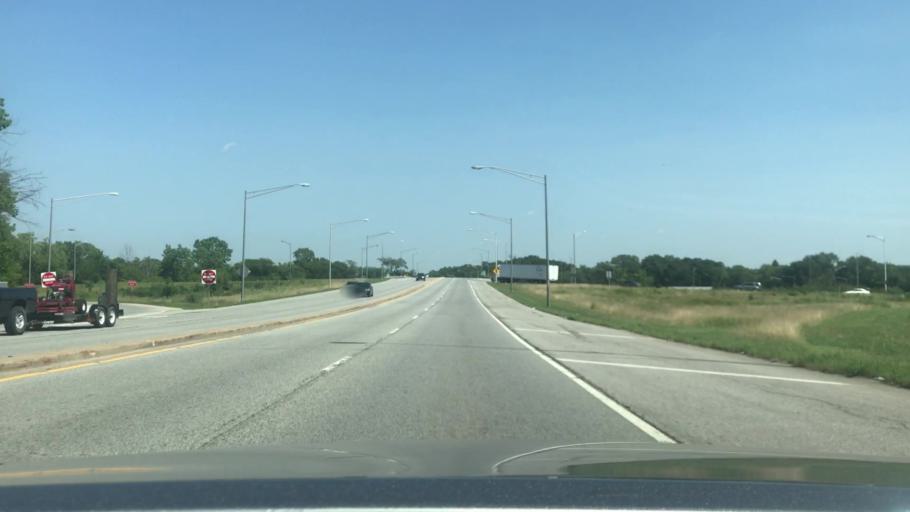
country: US
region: Illinois
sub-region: Cook County
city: Markham
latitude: 41.6030
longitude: -87.7129
